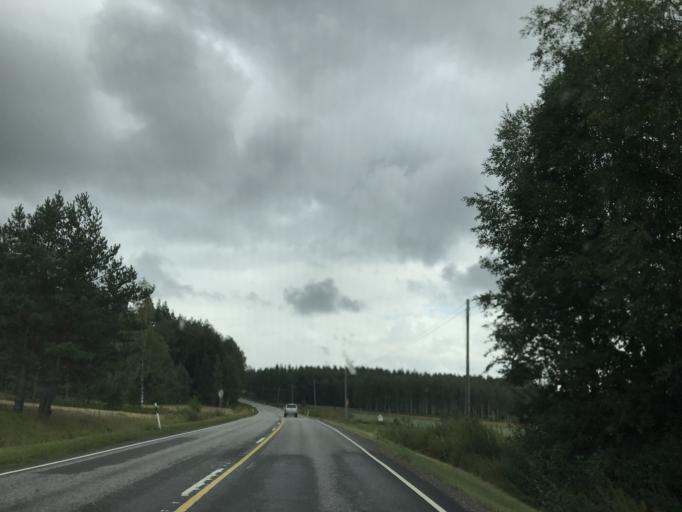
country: FI
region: Varsinais-Suomi
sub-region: Salo
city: Pernioe
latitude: 60.0865
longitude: 23.2299
